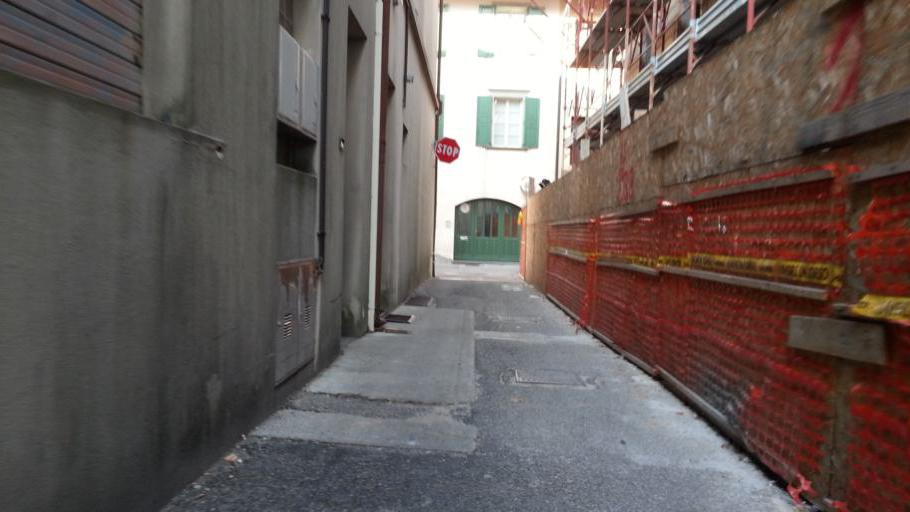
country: IT
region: Friuli Venezia Giulia
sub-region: Provincia di Udine
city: Venzone
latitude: 46.3348
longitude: 13.1405
